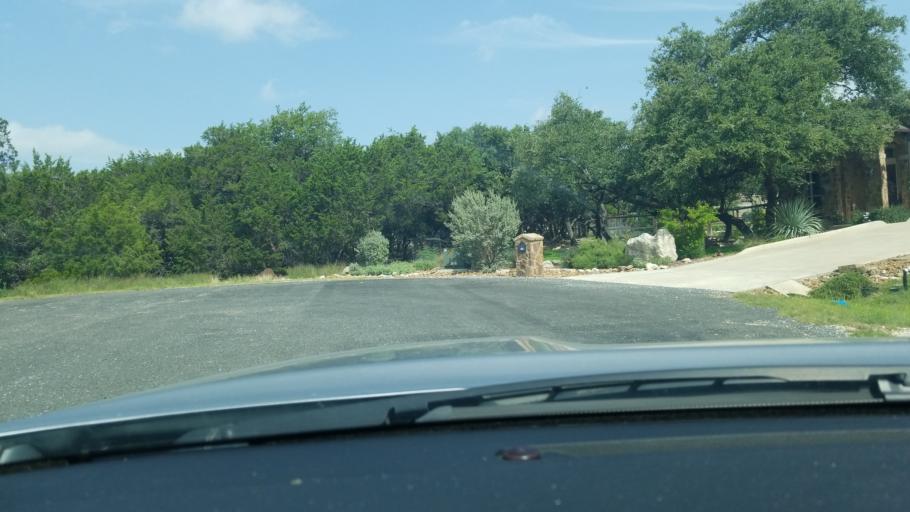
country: US
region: Texas
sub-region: Bexar County
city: Timberwood Park
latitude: 29.6999
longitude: -98.4923
